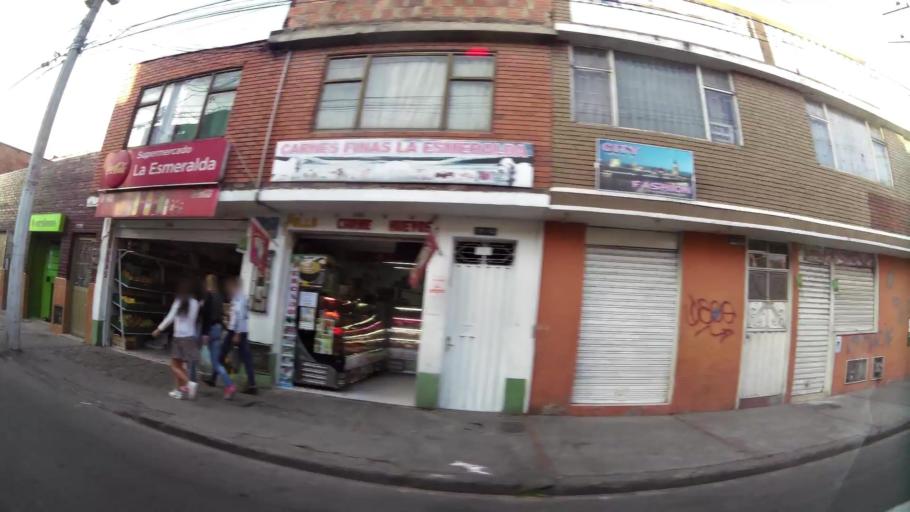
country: CO
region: Bogota D.C.
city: Bogota
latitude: 4.5664
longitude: -74.1317
